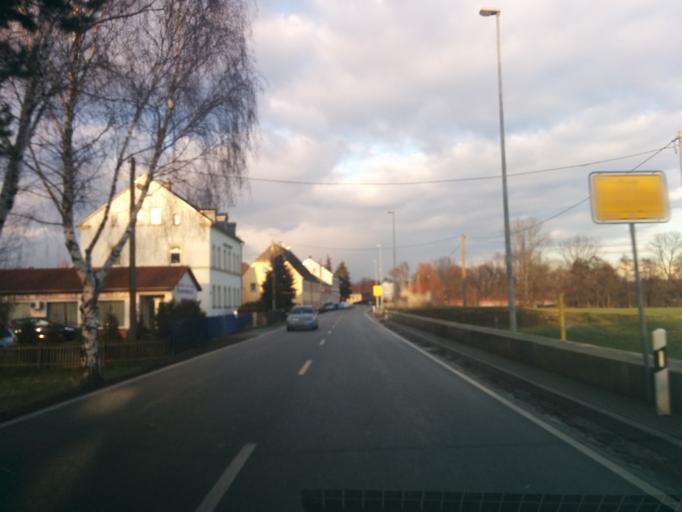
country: DE
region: Saxony
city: Niederwiesa
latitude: 50.8989
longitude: 13.0092
